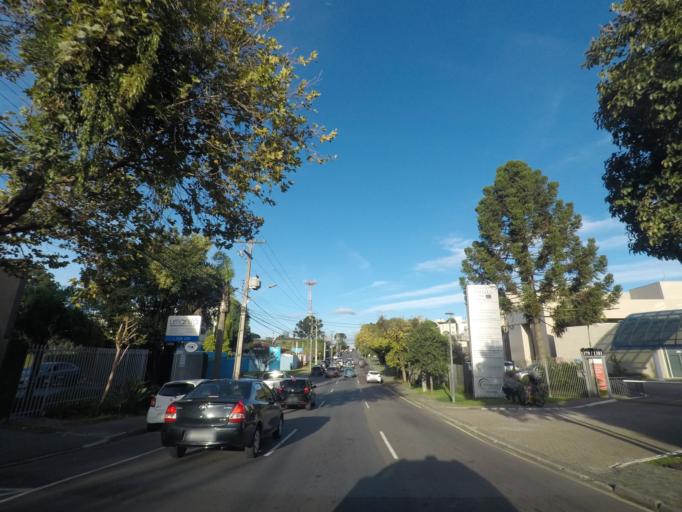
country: BR
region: Parana
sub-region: Curitiba
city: Curitiba
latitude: -25.4157
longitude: -49.2828
